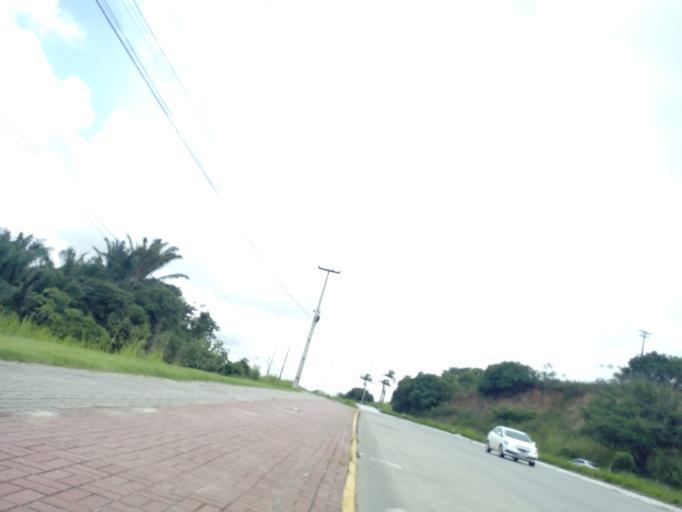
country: BR
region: Pernambuco
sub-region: Cabo De Santo Agostinho
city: Cabo
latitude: -8.2655
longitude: -35.0182
